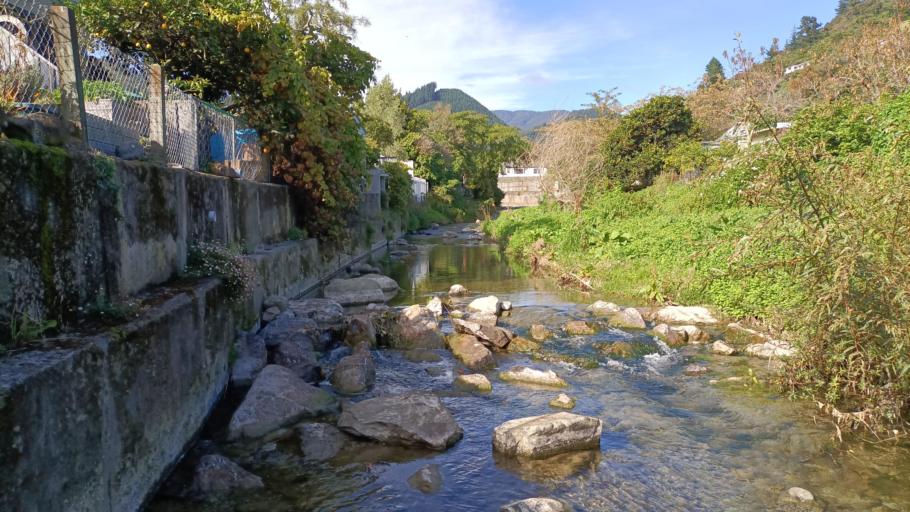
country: NZ
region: Nelson
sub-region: Nelson City
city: Nelson
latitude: -41.2808
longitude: 173.2908
